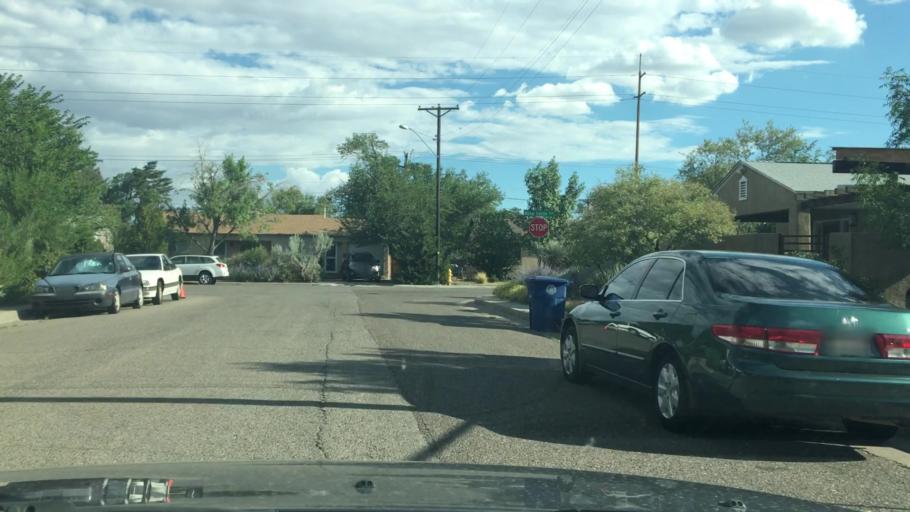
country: US
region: New Mexico
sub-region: Bernalillo County
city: Albuquerque
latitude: 35.0884
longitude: -106.6034
